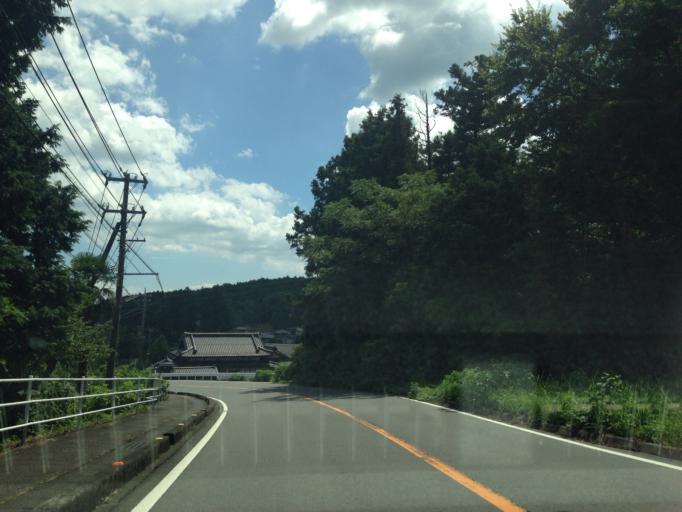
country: JP
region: Shizuoka
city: Gotemba
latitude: 35.2236
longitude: 138.8865
